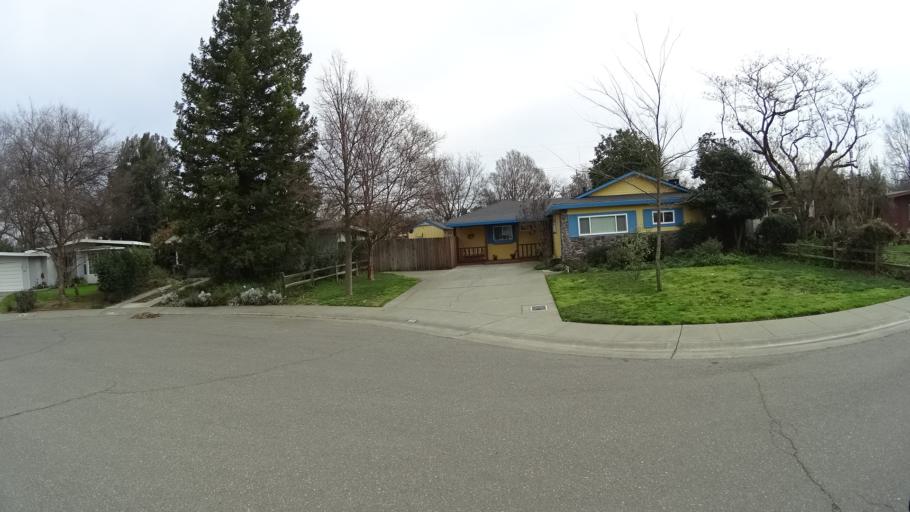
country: US
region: California
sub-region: Yolo County
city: Davis
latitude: 38.5551
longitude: -121.7300
